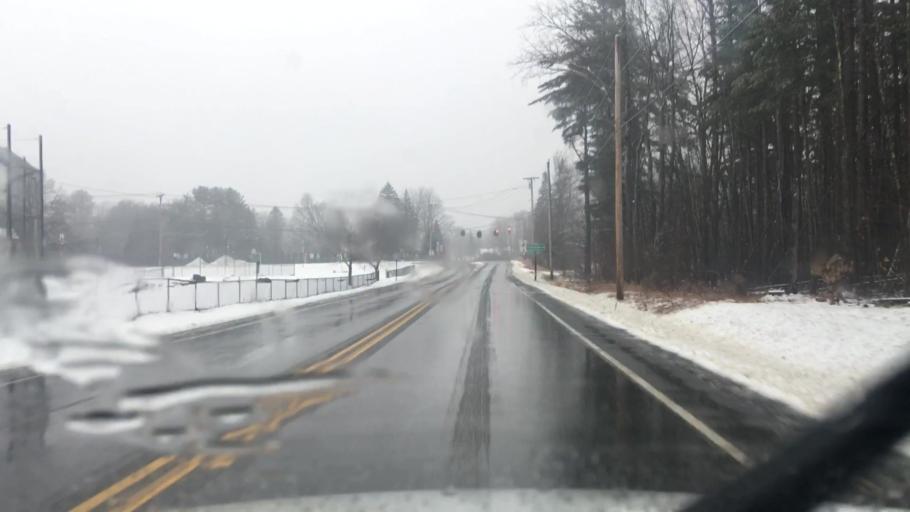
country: US
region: Maine
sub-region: York County
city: Buxton
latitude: 43.6031
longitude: -70.5359
